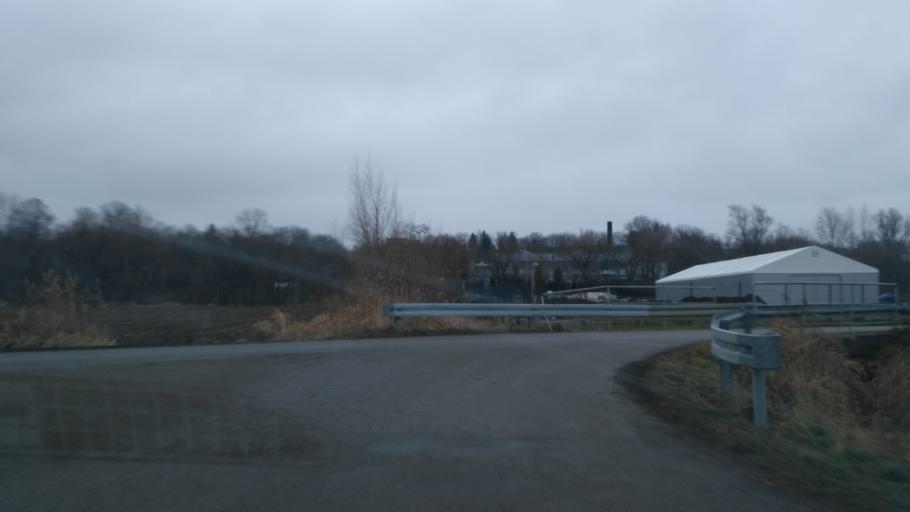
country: PL
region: Subcarpathian Voivodeship
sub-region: Powiat przeworski
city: Zarzecze
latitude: 49.9378
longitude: 22.5660
